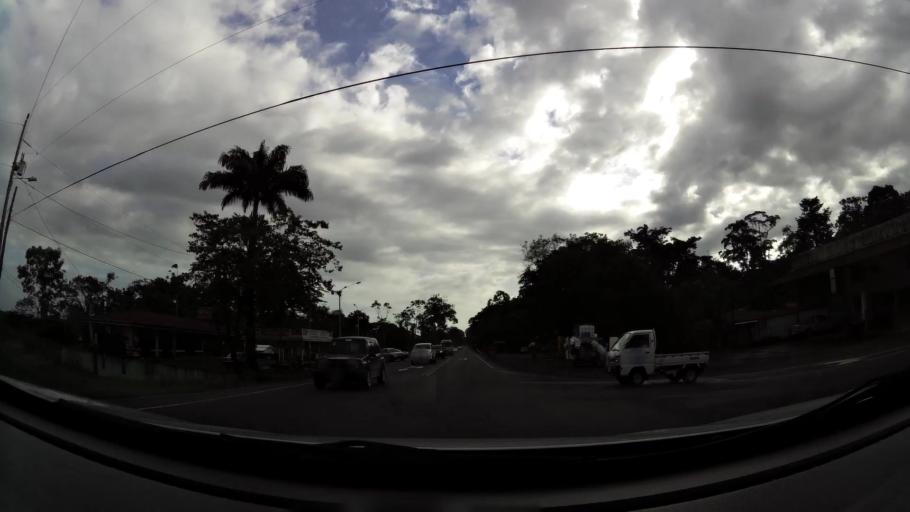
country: CR
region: Limon
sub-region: Canton de Pococi
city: Guapiles
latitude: 10.2051
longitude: -83.7426
